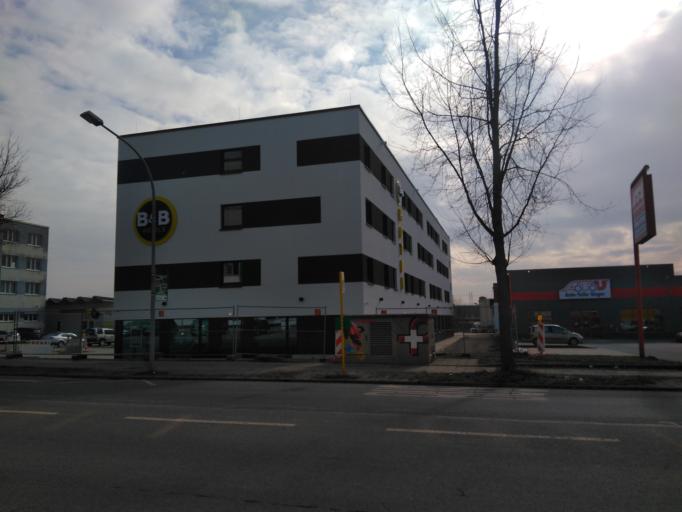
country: DE
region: Thuringia
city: Weimar
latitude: 50.9938
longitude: 11.3261
